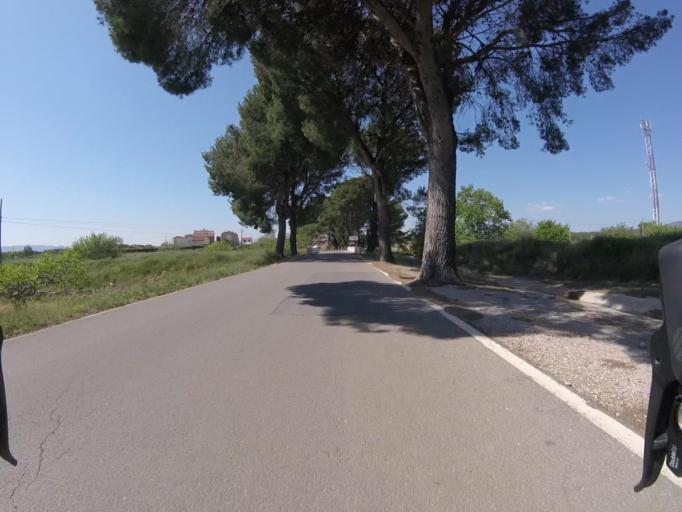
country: ES
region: Valencia
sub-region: Provincia de Castello
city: Benlloch
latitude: 40.2142
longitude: 0.0317
